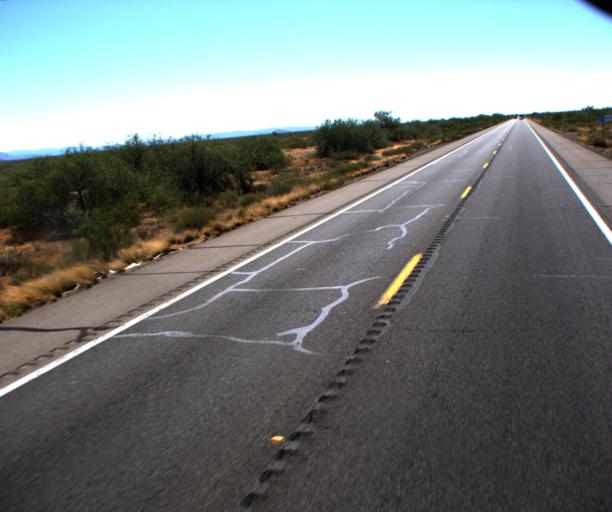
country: US
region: Arizona
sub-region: Yavapai County
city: Congress
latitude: 34.1132
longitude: -112.9358
